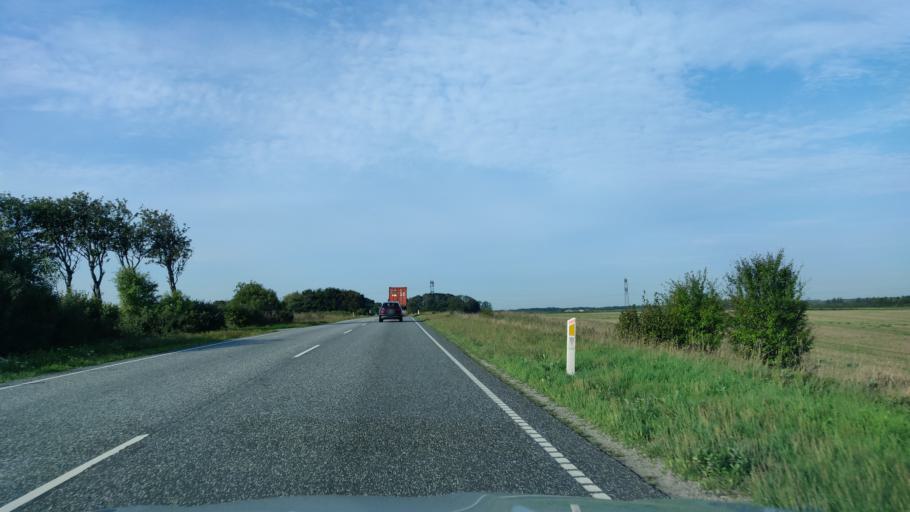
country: DK
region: North Denmark
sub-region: Vesthimmerland Kommune
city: Aars
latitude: 56.7973
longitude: 9.6302
